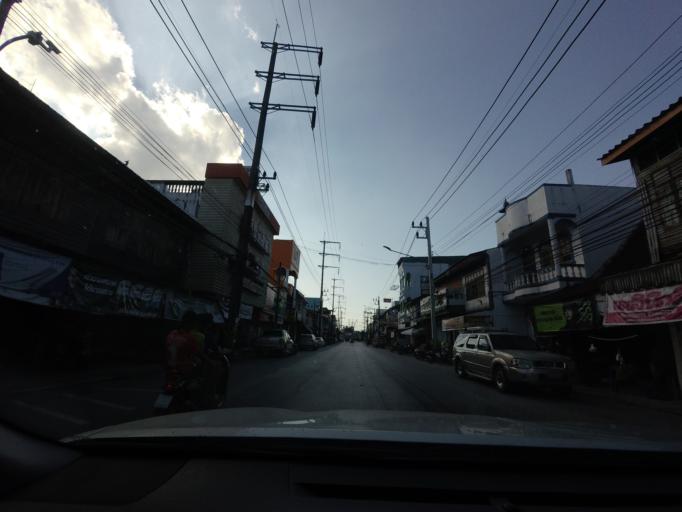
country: TH
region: Phangnga
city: Thai Mueang
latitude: 8.2775
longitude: 98.3071
